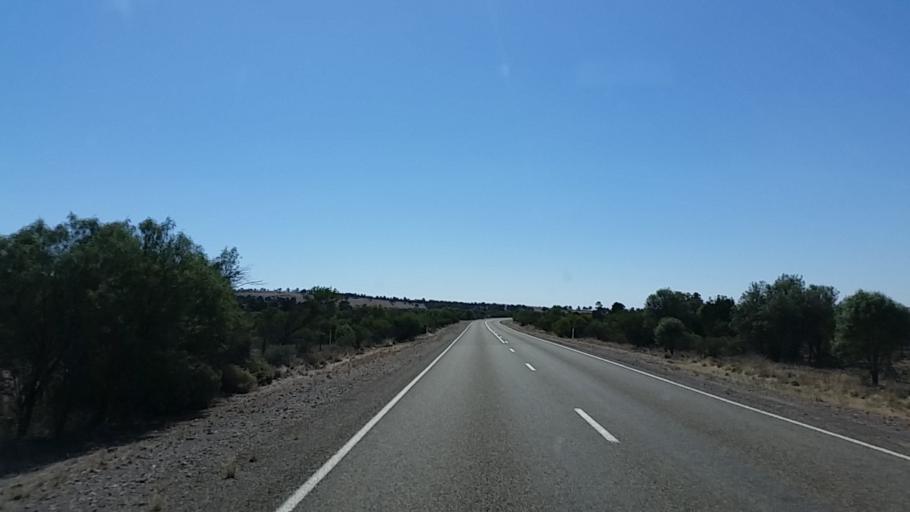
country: AU
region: South Australia
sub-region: Flinders Ranges
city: Quorn
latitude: -32.5131
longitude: 138.5474
